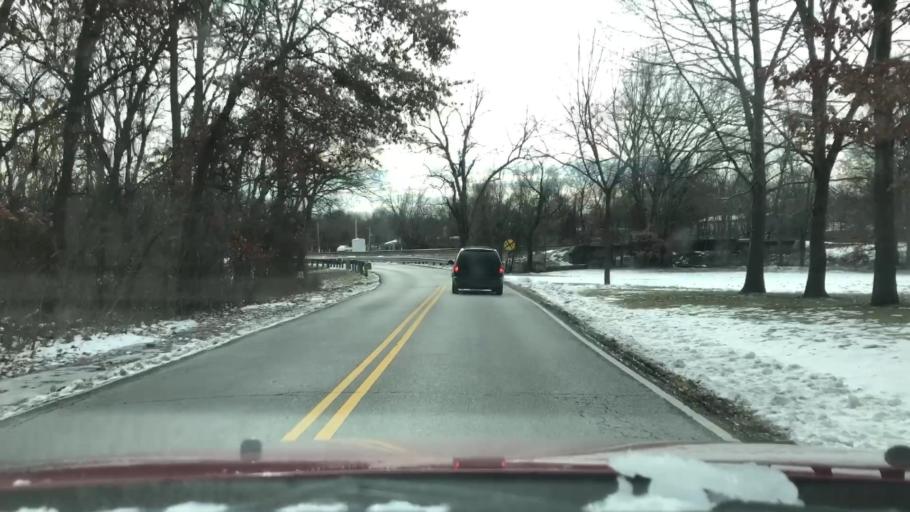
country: US
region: Missouri
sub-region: Jackson County
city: Greenwood
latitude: 38.8575
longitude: -94.3429
